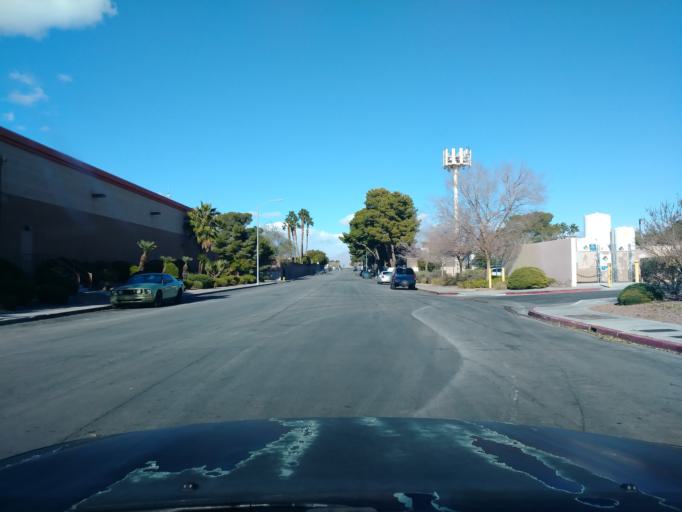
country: US
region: Nevada
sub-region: Clark County
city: Spring Valley
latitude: 36.1454
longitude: -115.2124
